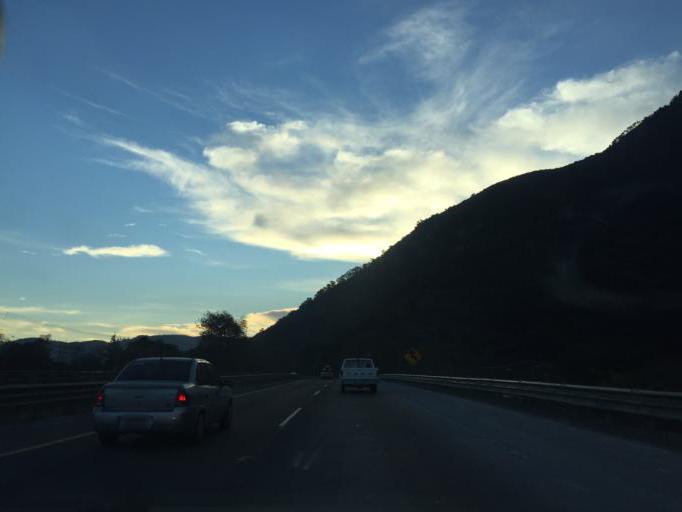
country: MX
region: Veracruz
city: Rio Blanco
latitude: 18.8281
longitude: -97.1197
